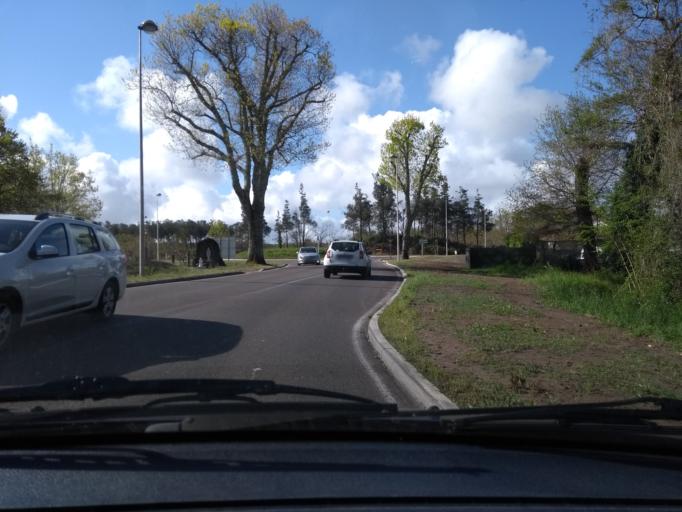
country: FR
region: Aquitaine
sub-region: Departement des Landes
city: Parentis-en-Born
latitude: 44.3410
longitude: -1.0808
